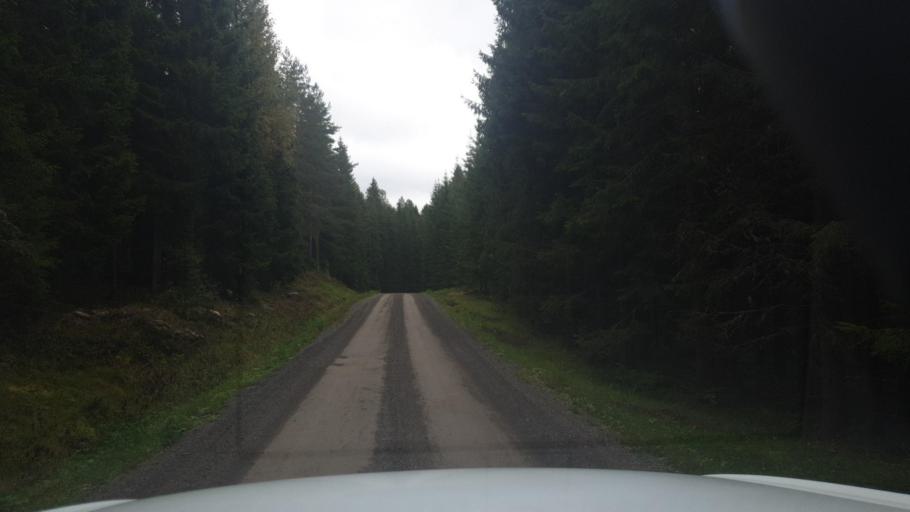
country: SE
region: Vaermland
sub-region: Sunne Kommun
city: Sunne
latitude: 59.8589
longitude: 12.8402
